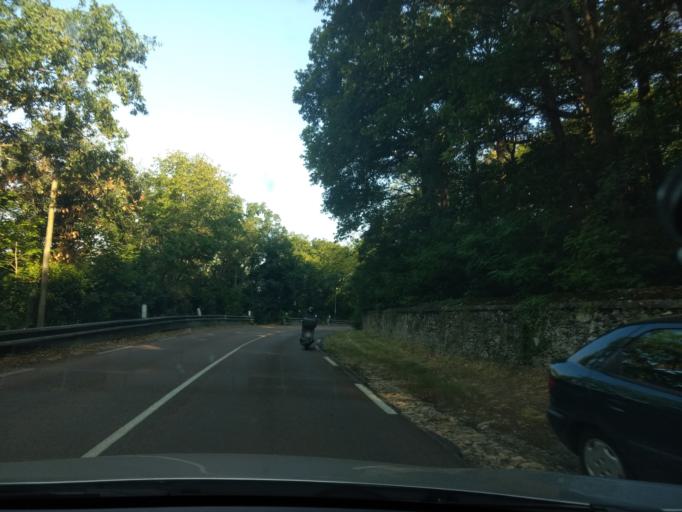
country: FR
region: Ile-de-France
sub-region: Departement de l'Essonne
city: Bievres
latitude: 48.7597
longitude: 2.2024
